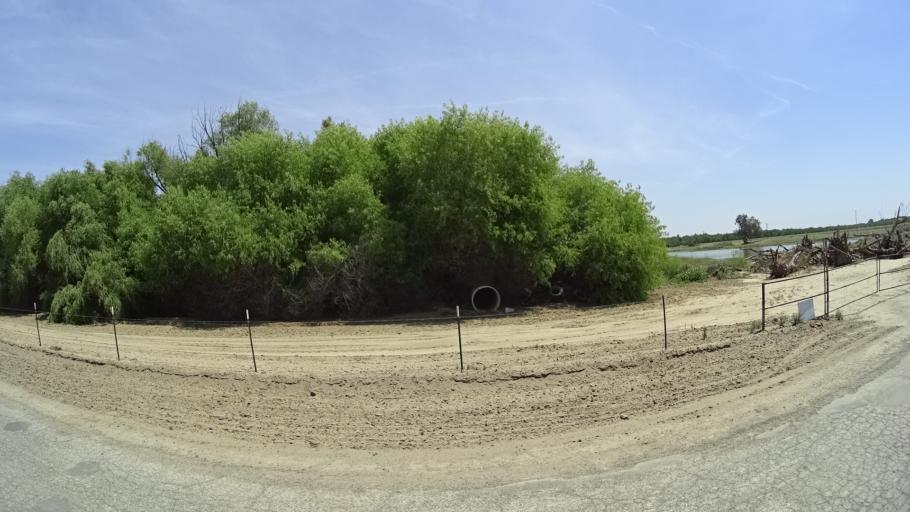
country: US
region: California
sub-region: Fresno County
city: Riverdale
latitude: 36.3969
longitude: -119.8162
